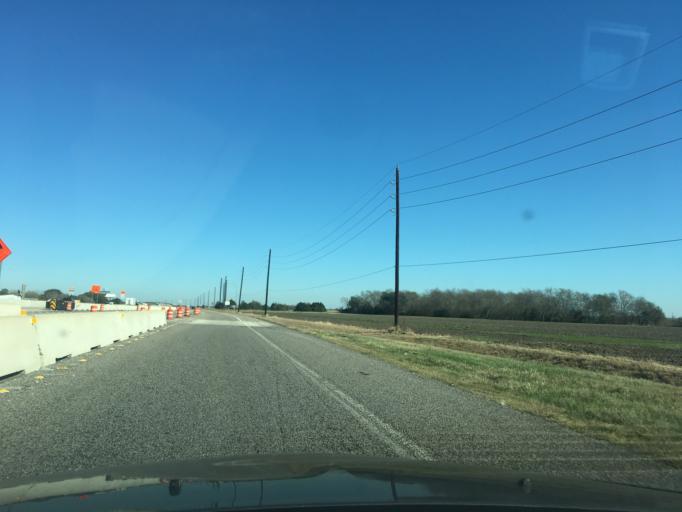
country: US
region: Texas
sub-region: Fort Bend County
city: Pleak
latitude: 29.4893
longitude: -95.9229
